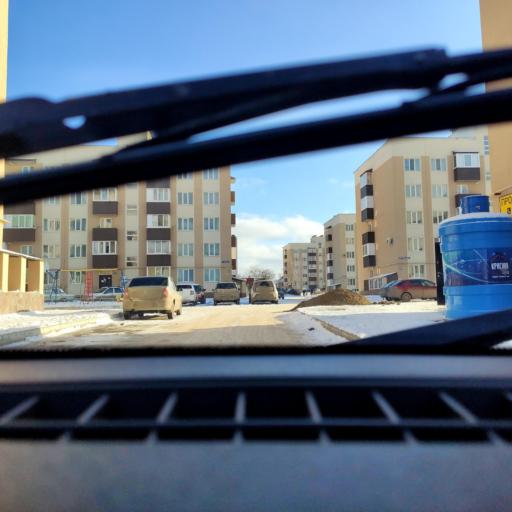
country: RU
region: Bashkortostan
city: Iglino
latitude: 54.8178
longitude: 56.3958
